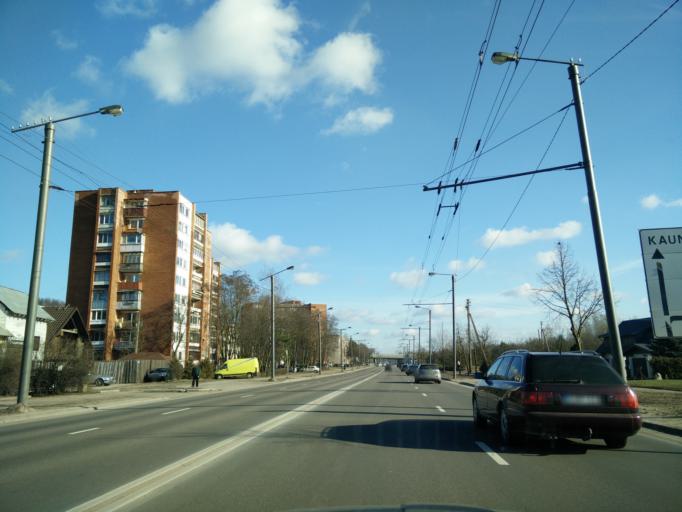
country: LT
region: Kauno apskritis
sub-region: Kauno rajonas
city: Akademija (Kaunas)
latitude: 54.9187
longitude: 23.8302
